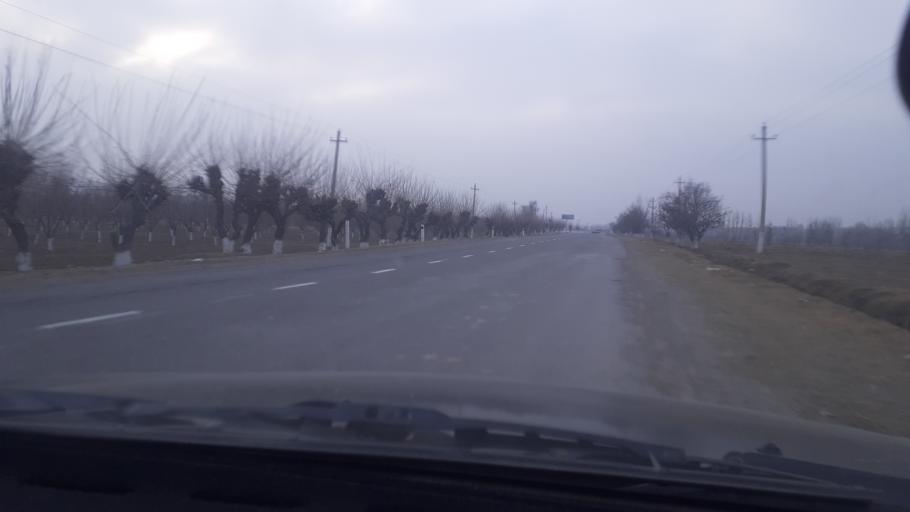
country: UZ
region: Namangan
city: Yangiqo`rg`on
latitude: 41.2415
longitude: 71.6920
